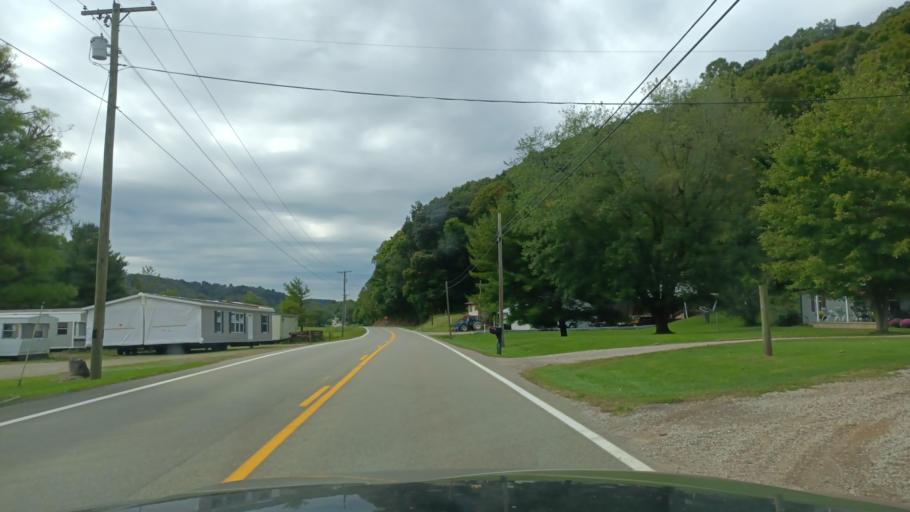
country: US
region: Ohio
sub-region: Vinton County
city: McArthur
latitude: 39.2720
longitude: -82.5975
